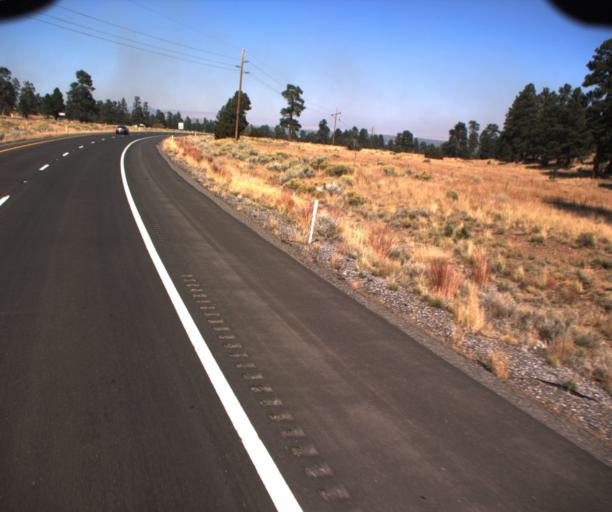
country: US
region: Arizona
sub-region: Coconino County
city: Flagstaff
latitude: 35.3809
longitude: -111.5803
